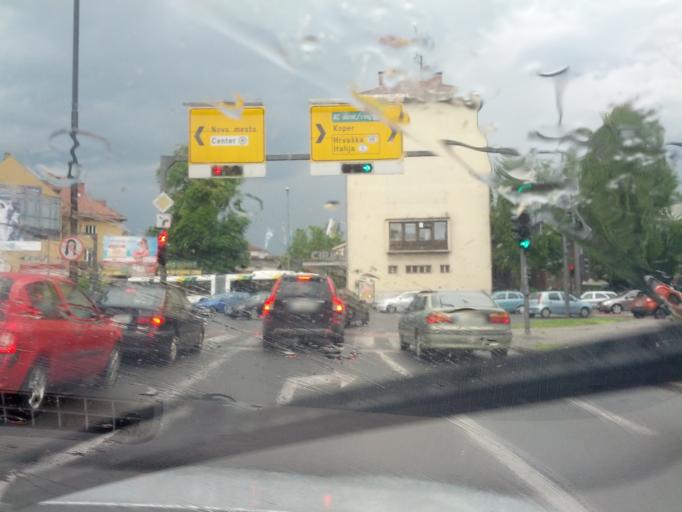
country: SI
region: Ljubljana
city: Ljubljana
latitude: 46.0477
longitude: 14.4948
